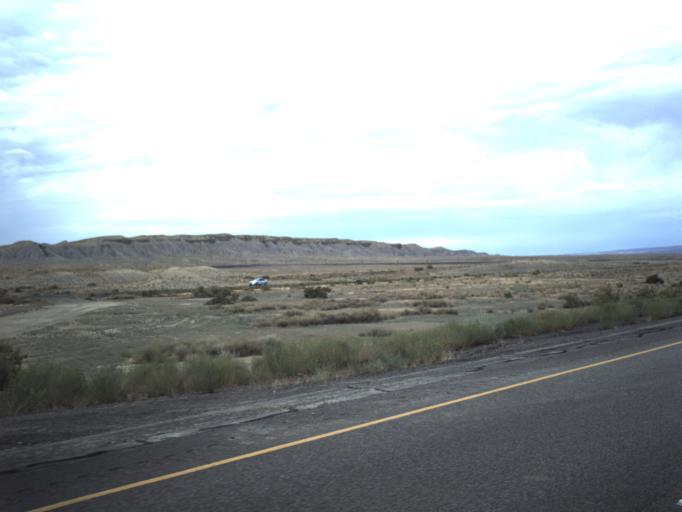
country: US
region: Utah
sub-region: Grand County
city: Moab
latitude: 38.9371
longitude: -109.4856
